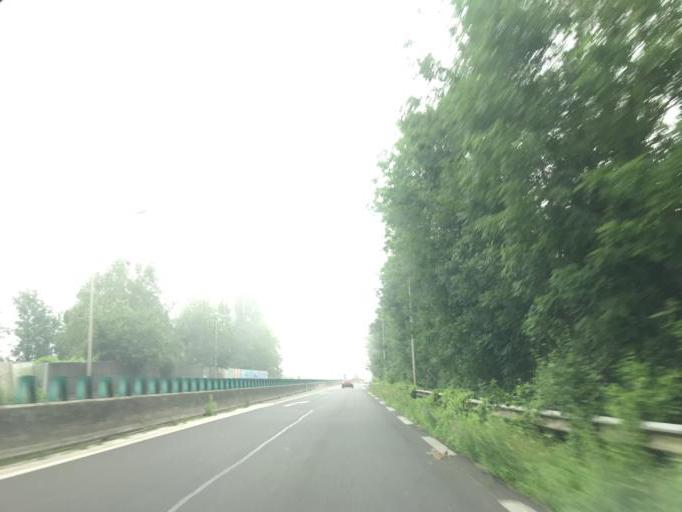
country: FR
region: Ile-de-France
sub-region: Departement de Seine-et-Marne
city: Lagny-sur-Marne
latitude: 48.8757
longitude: 2.7205
